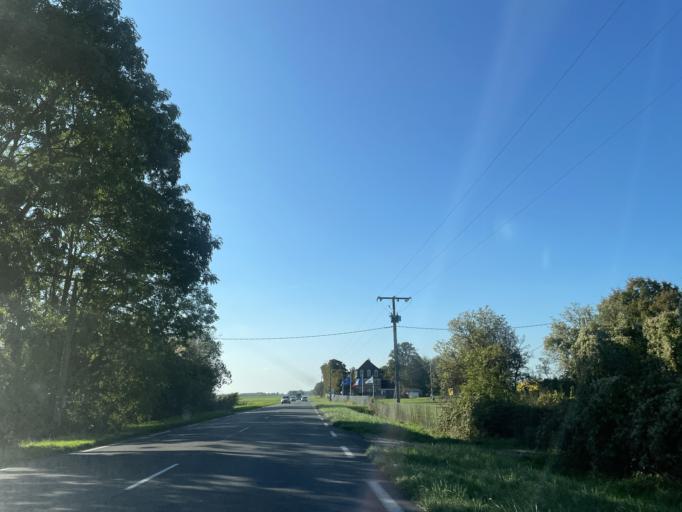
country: FR
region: Ile-de-France
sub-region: Departement de Seine-et-Marne
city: Pommeuse
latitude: 48.8315
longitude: 3.0122
